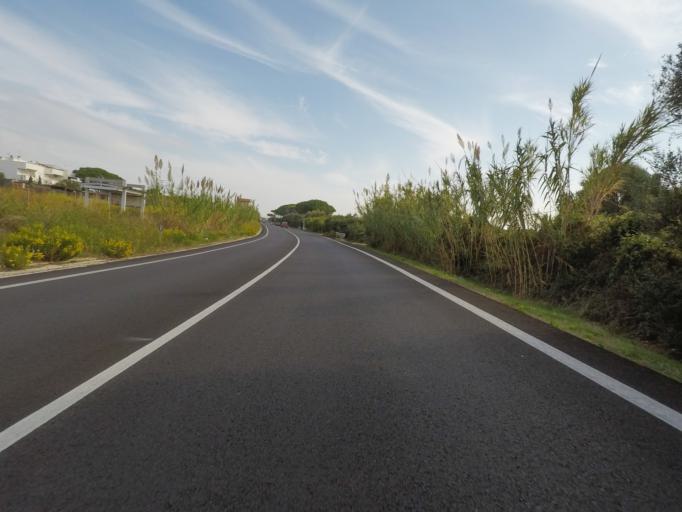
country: IT
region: Latium
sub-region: Citta metropolitana di Roma Capitale
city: Civitavecchia
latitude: 42.0483
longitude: 11.8212
